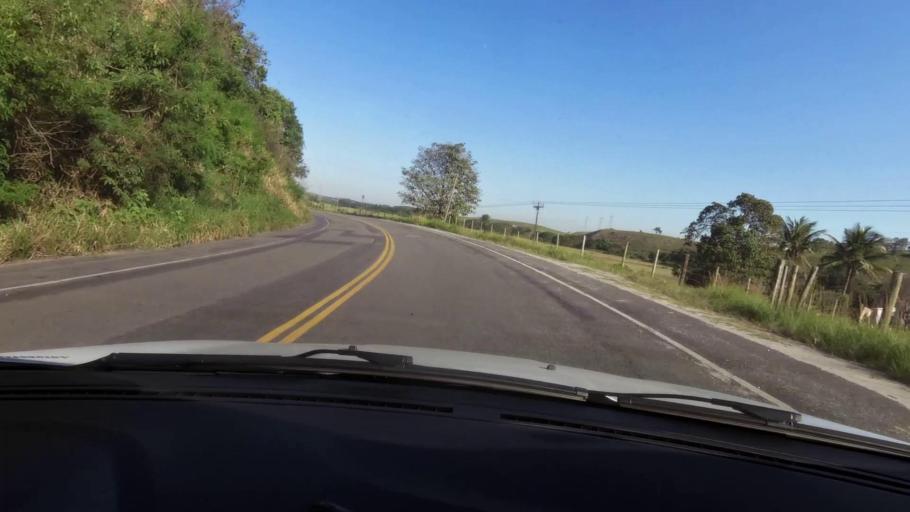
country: BR
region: Espirito Santo
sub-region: Alfredo Chaves
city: Alfredo Chaves
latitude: -20.7114
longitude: -40.6695
